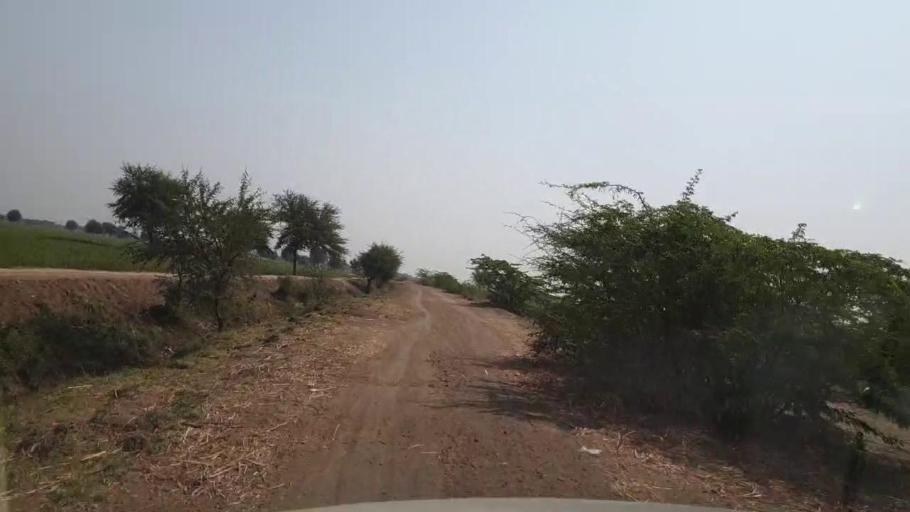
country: PK
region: Sindh
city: Chor
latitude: 25.4538
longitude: 69.6871
